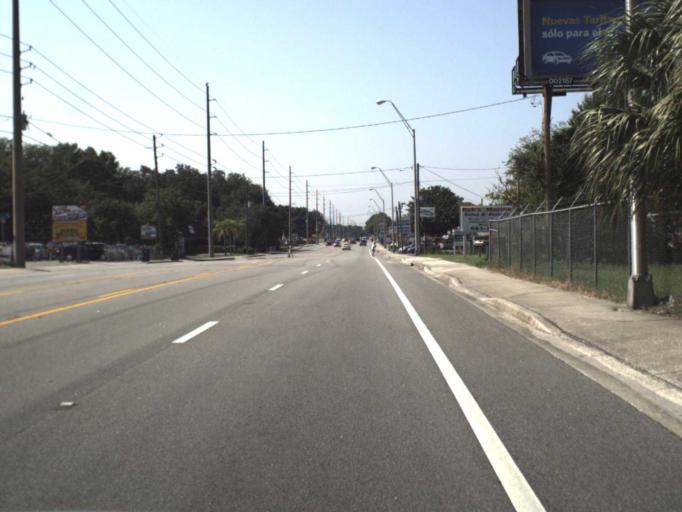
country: US
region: Florida
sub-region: Hillsborough County
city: Lake Magdalene
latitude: 28.0765
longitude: -82.4595
